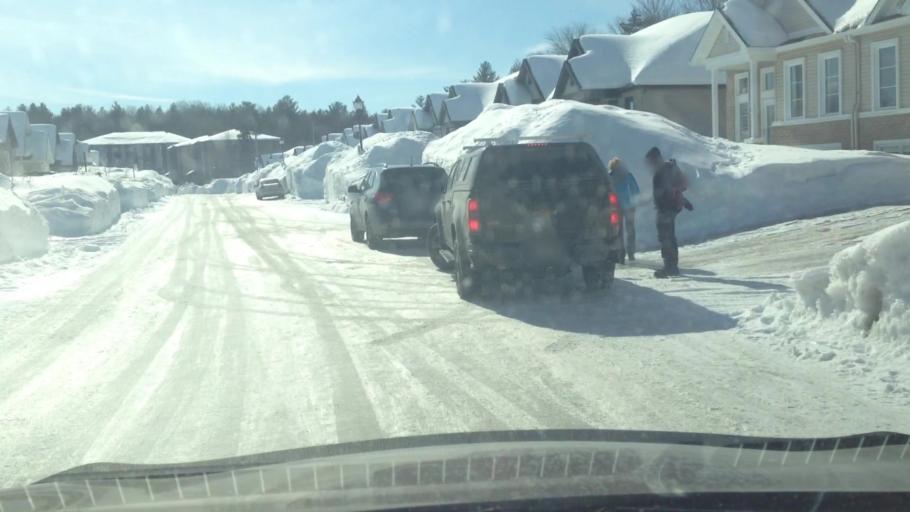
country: CA
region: Quebec
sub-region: Laurentides
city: Saint-Jerome
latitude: 45.7814
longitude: -73.9703
